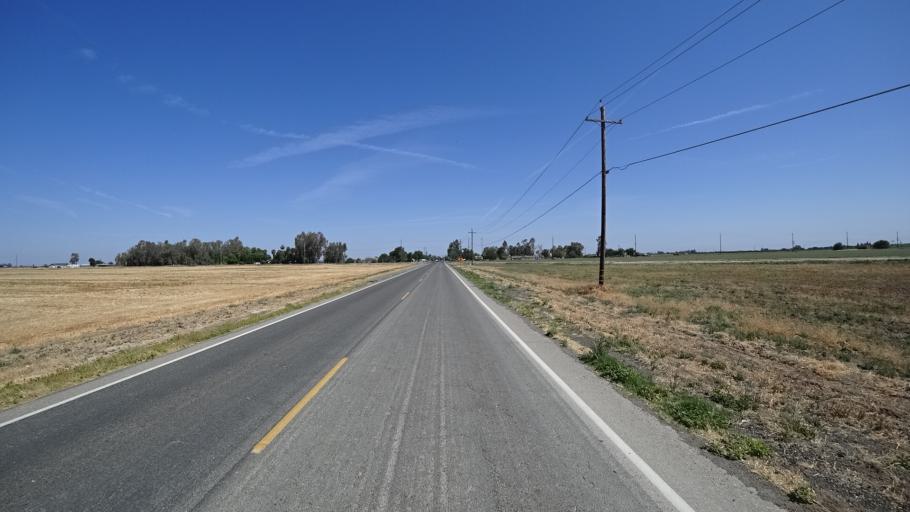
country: US
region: California
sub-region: Kings County
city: Lemoore
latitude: 36.2372
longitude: -119.7806
